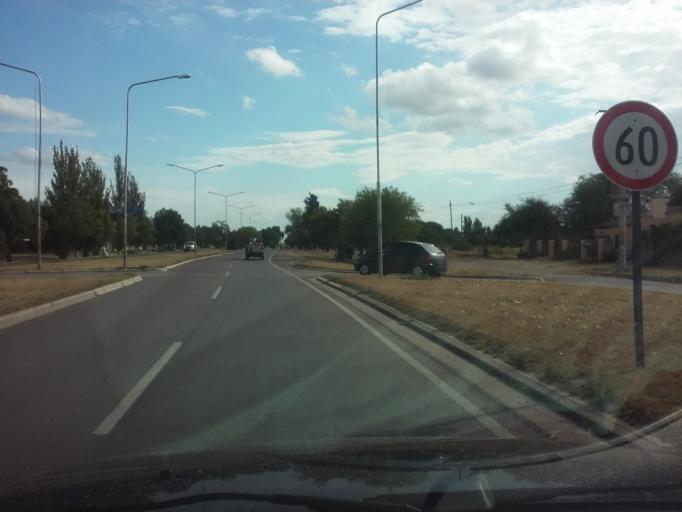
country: AR
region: La Pampa
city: Santa Rosa
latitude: -36.6383
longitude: -64.3201
